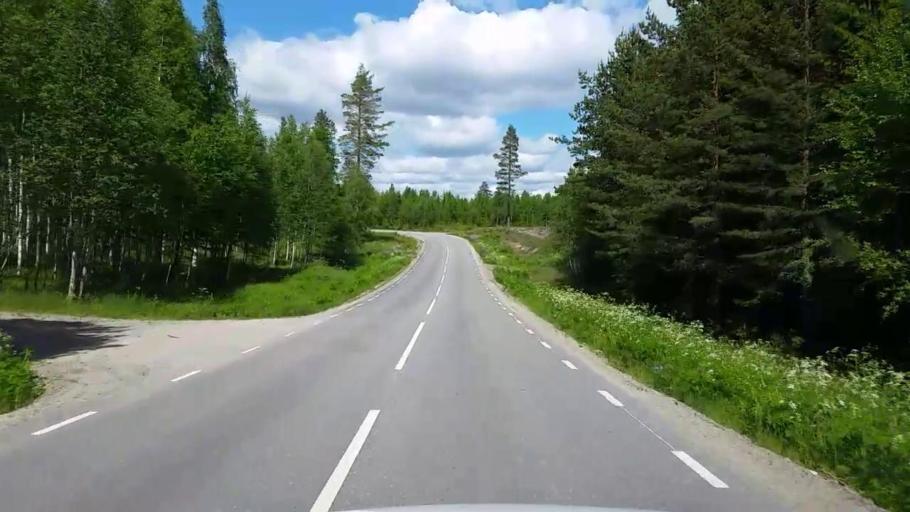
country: SE
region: Gaevleborg
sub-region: Ovanakers Kommun
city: Alfta
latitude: 61.2624
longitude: 16.1226
